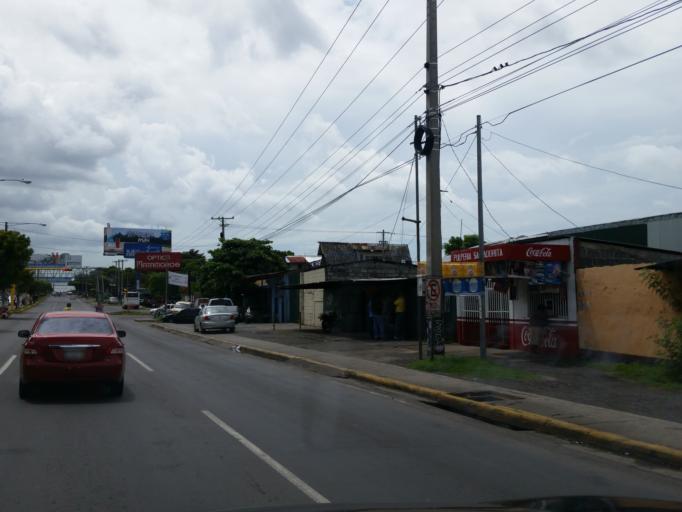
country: NI
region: Managua
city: Managua
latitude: 12.1474
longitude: -86.1889
